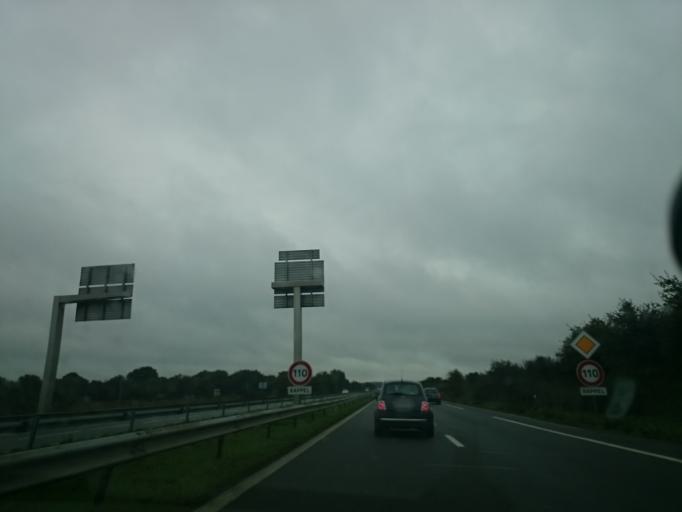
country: FR
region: Brittany
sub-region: Departement du Morbihan
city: Peaule
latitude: 47.5370
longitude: -2.3930
